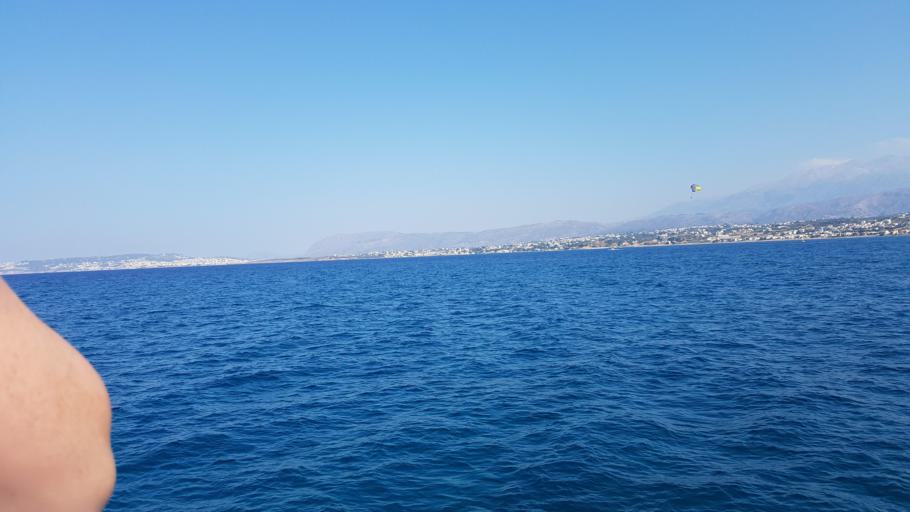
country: GR
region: Crete
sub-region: Nomos Chanias
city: Agia Marina
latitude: 35.5318
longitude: 23.9351
